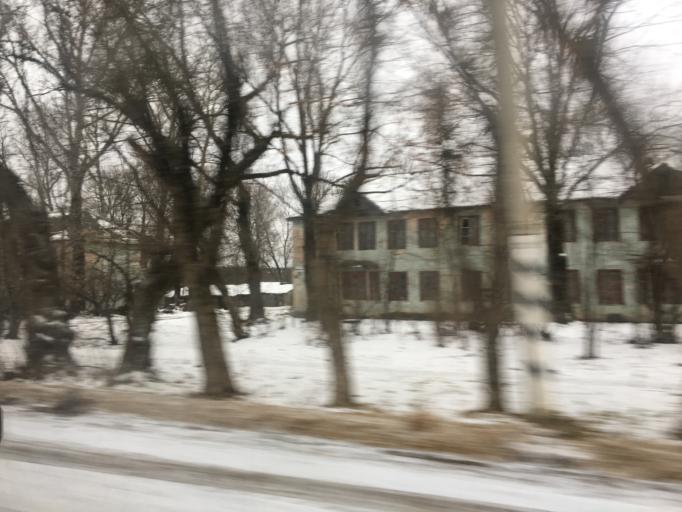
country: RU
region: Tula
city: Pervomayskiy
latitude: 54.0496
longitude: 37.5301
